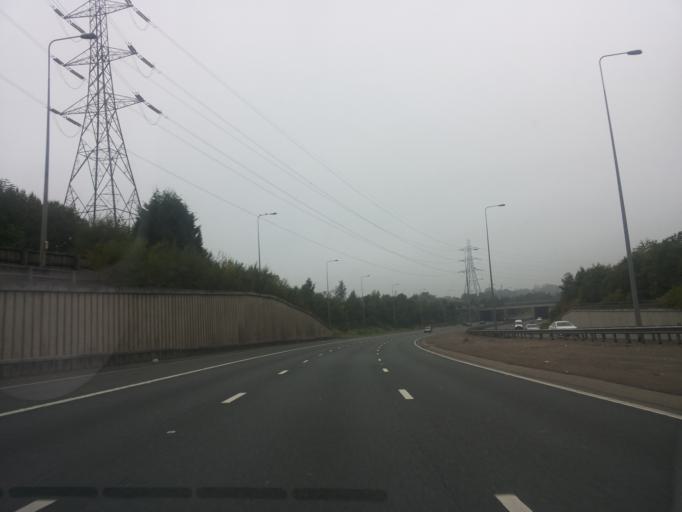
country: GB
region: England
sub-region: Borough of Rochdale
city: Middleton
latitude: 53.5323
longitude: -2.2027
